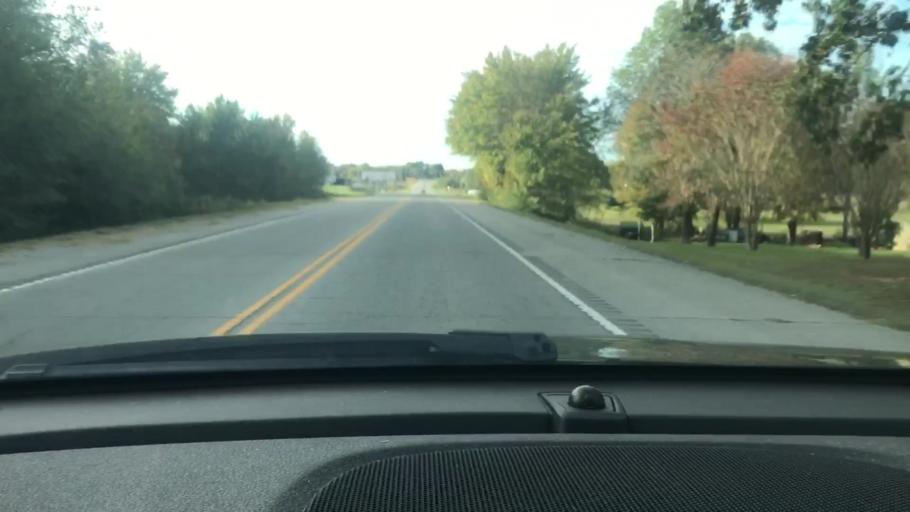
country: US
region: Tennessee
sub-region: Dickson County
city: White Bluff
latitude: 36.1288
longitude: -87.2297
